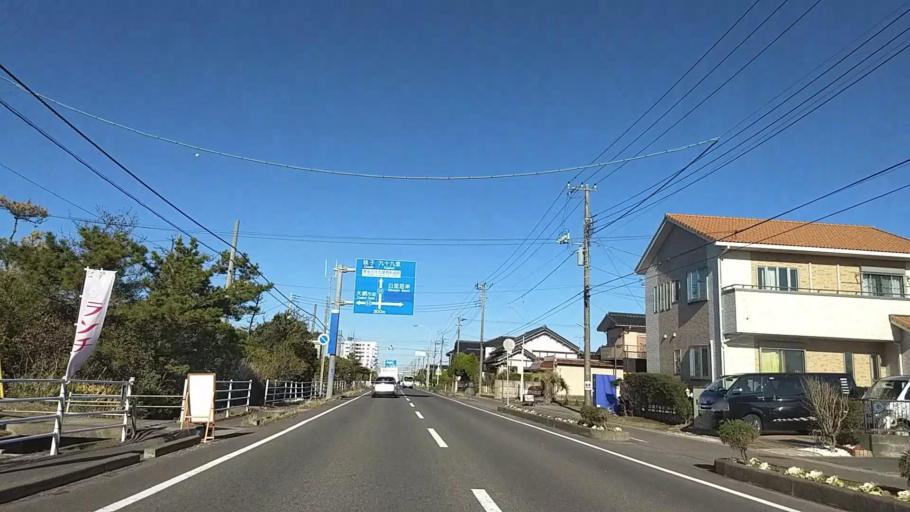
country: JP
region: Chiba
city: Togane
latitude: 35.4830
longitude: 140.4188
